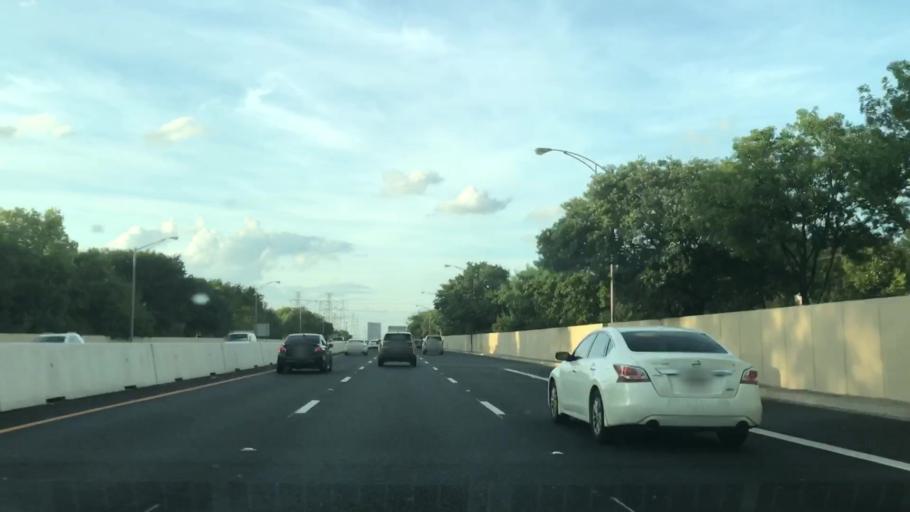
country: US
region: Texas
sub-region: Dallas County
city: University Park
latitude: 32.8974
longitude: -96.8101
